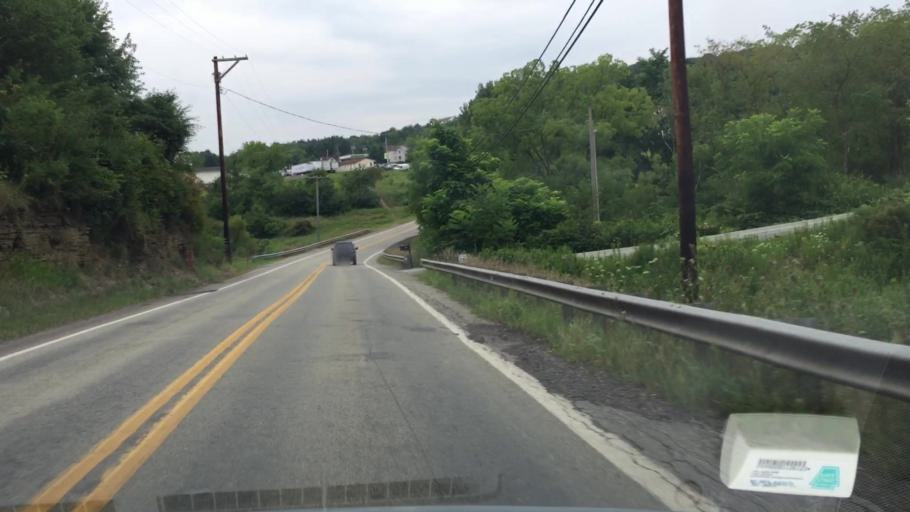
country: US
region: Pennsylvania
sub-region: Allegheny County
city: Curtisville
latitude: 40.6320
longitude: -79.8543
